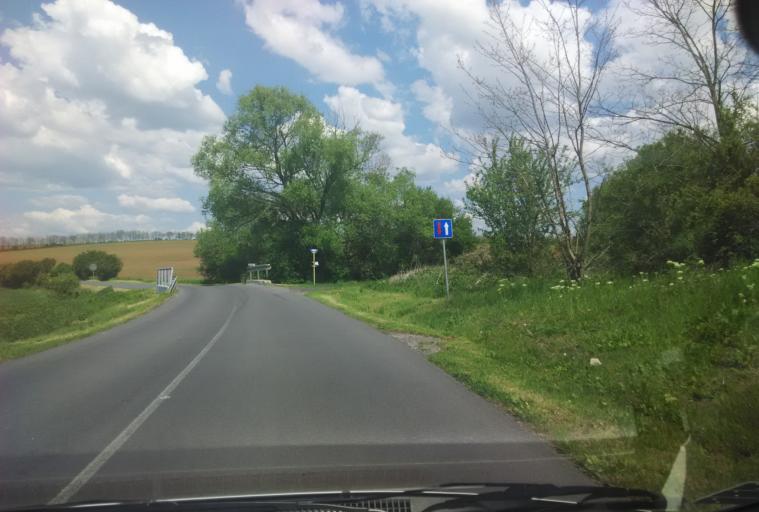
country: SK
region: Banskobystricky
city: Dudince
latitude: 48.1720
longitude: 18.8577
